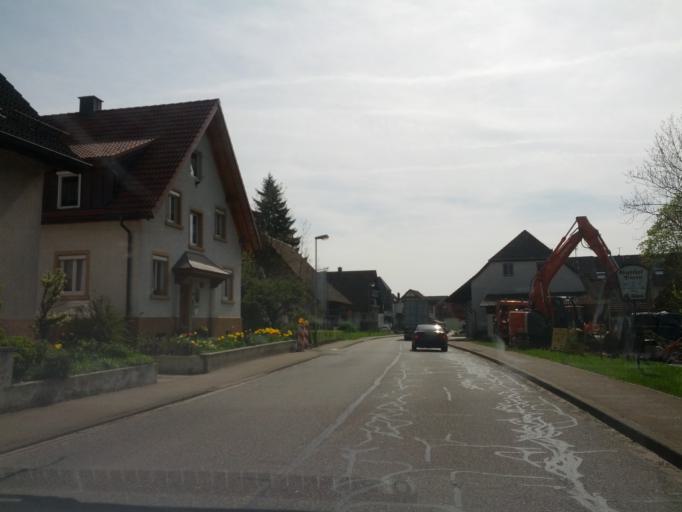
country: DE
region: Baden-Wuerttemberg
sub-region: Freiburg Region
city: Gutach im Breisgau
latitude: 48.1446
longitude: 8.0252
